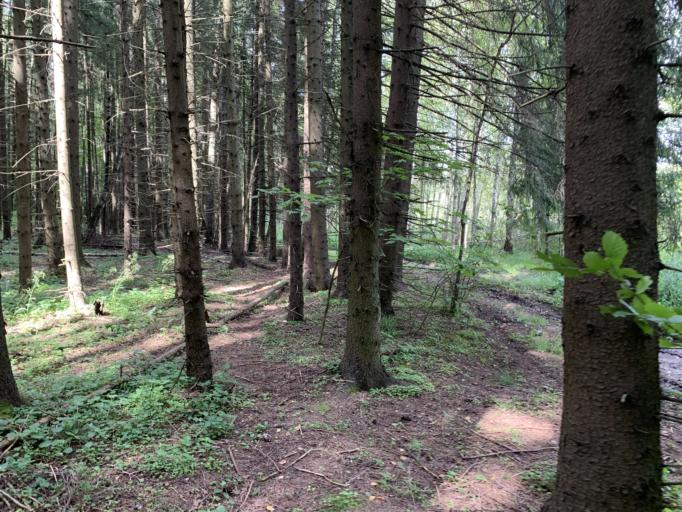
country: RU
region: Moskovskaya
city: Podosinki
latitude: 56.1789
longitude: 37.5678
